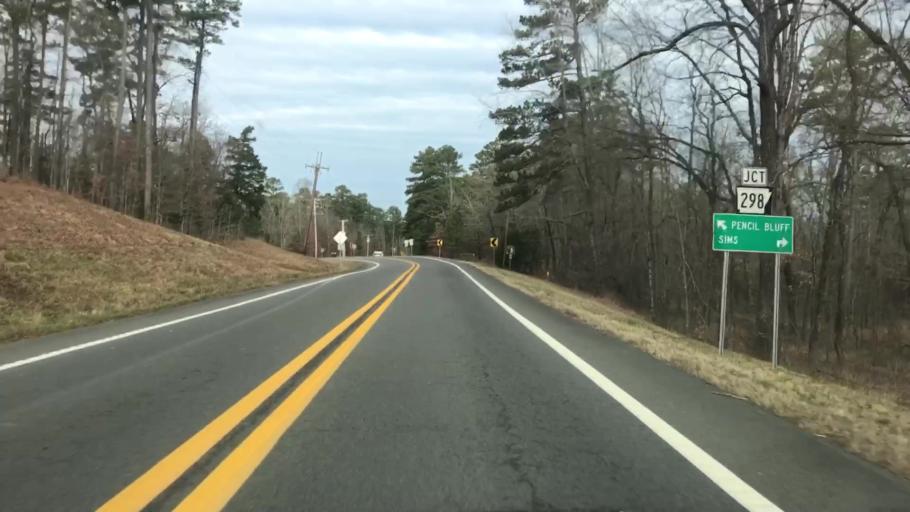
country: US
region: Arkansas
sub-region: Montgomery County
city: Mount Ida
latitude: 34.6075
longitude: -93.6728
